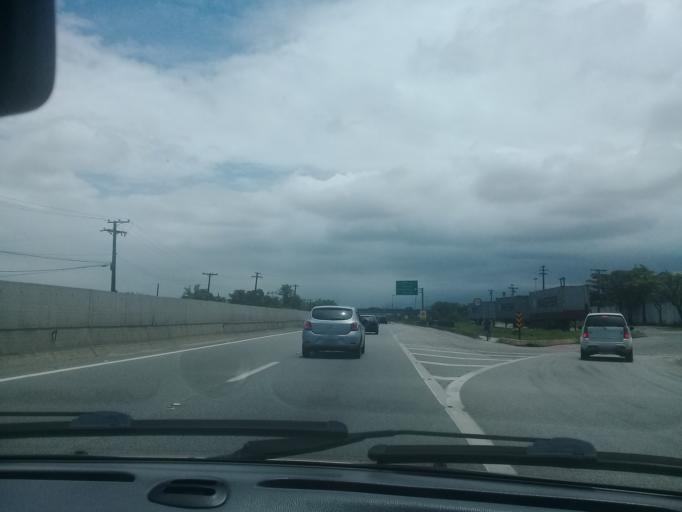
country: BR
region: Sao Paulo
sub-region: Guaruja
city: Guaruja
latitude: -23.9737
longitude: -46.2687
